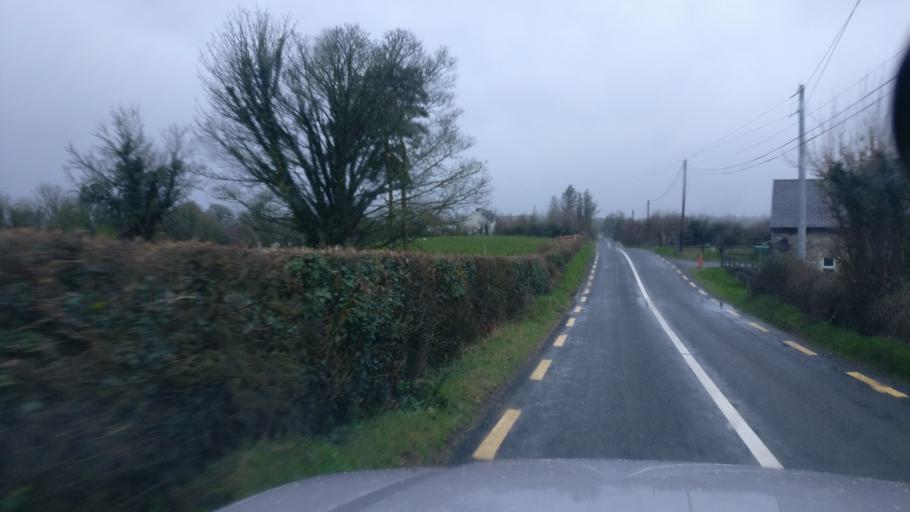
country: IE
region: Connaught
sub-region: County Galway
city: Portumna
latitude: 53.1009
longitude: -8.4027
